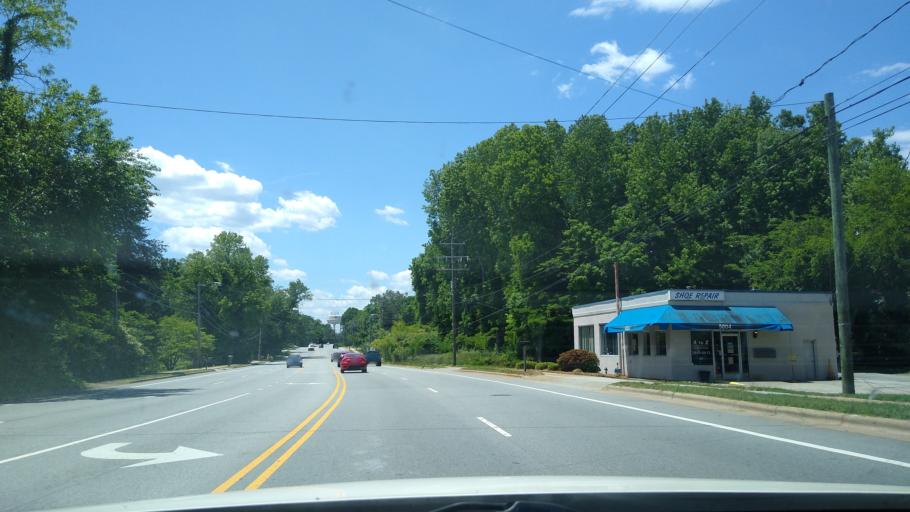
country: US
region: North Carolina
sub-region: Guilford County
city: Greensboro
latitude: 36.0921
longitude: -79.8719
